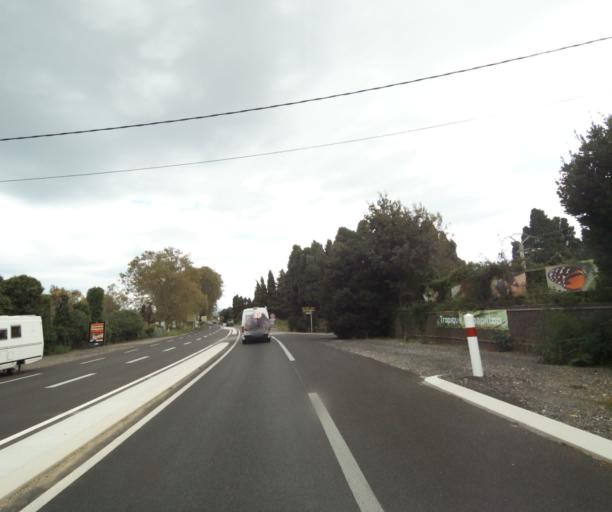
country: FR
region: Languedoc-Roussillon
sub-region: Departement des Pyrenees-Orientales
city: Elne
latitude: 42.5926
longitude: 2.9785
